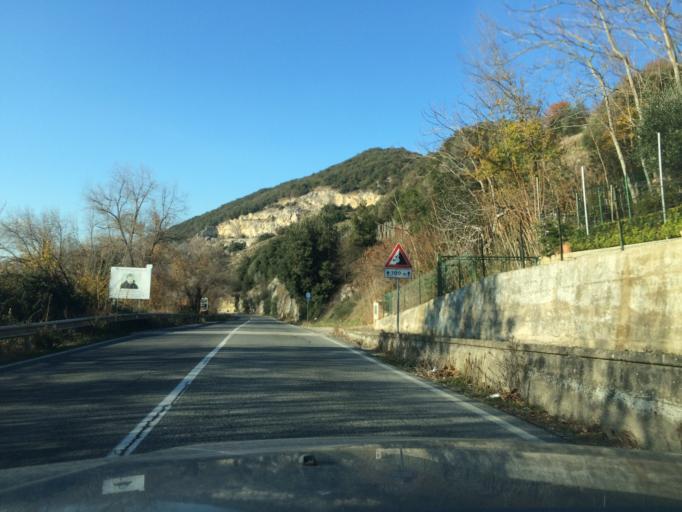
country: IT
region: Umbria
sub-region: Provincia di Terni
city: Fornole
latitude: 42.5399
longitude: 12.4680
